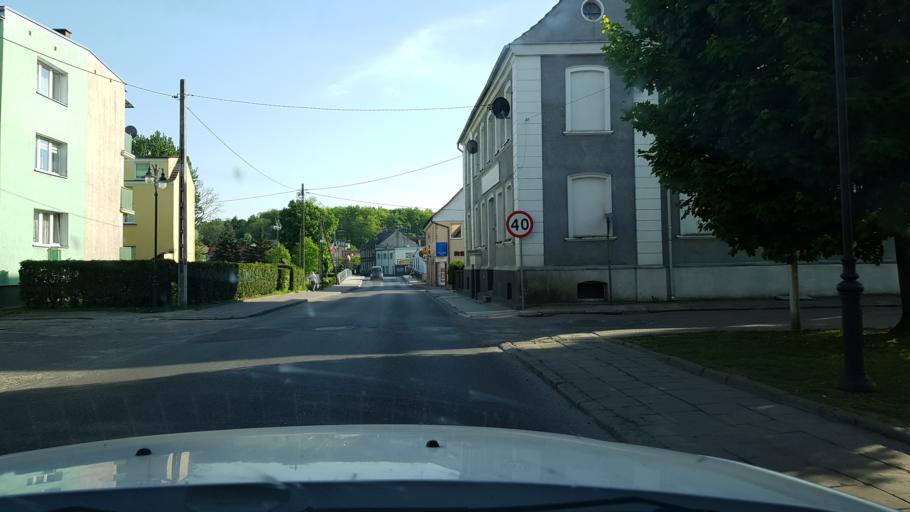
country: PL
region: West Pomeranian Voivodeship
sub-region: Powiat lobeski
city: Resko
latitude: 53.7722
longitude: 15.4042
